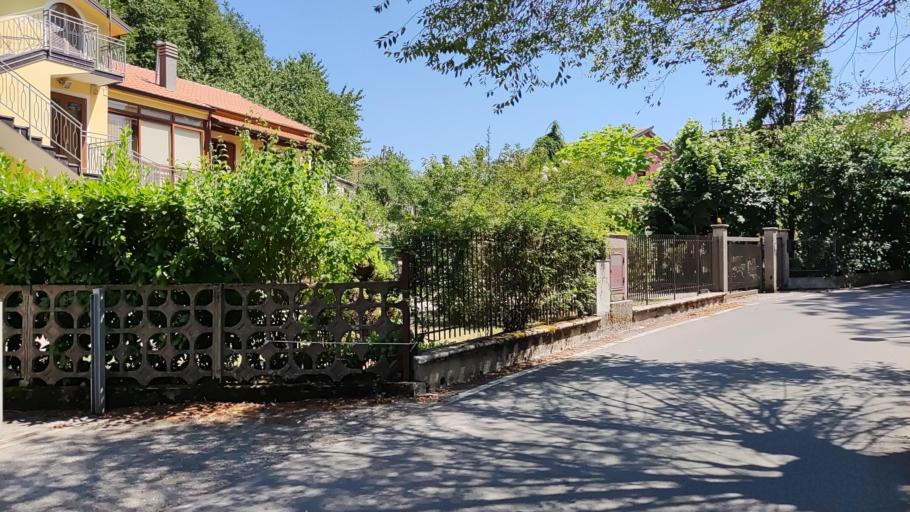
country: IT
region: Basilicate
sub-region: Provincia di Potenza
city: Nemoli
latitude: 40.0922
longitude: 15.8102
